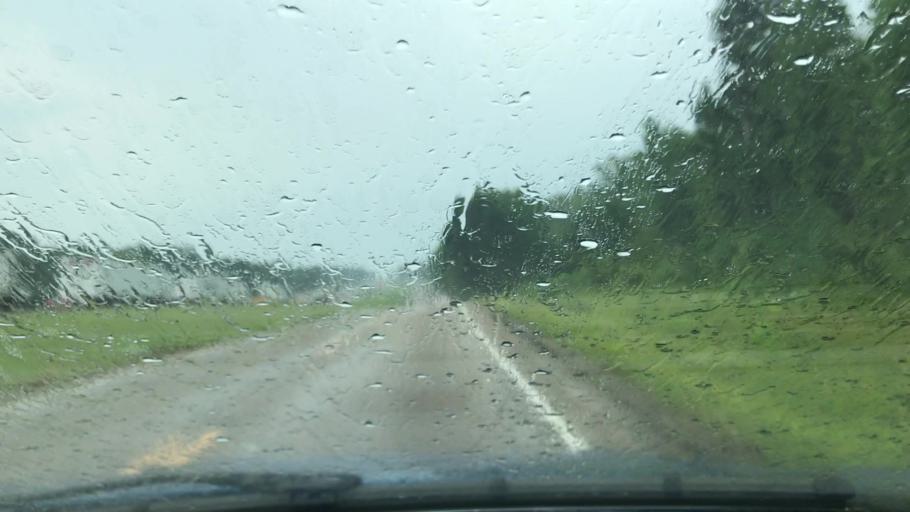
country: US
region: Texas
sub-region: Harrison County
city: Waskom
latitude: 32.4881
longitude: -94.1370
